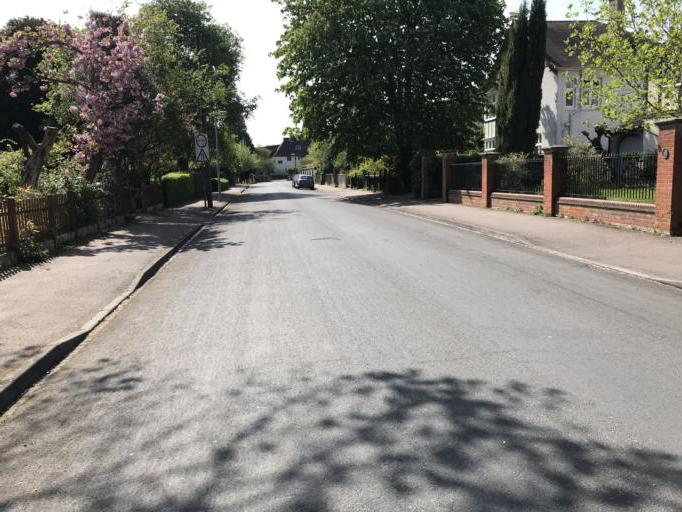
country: GB
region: England
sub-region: Cambridgeshire
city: Cambridge
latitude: 52.2165
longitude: 0.1009
